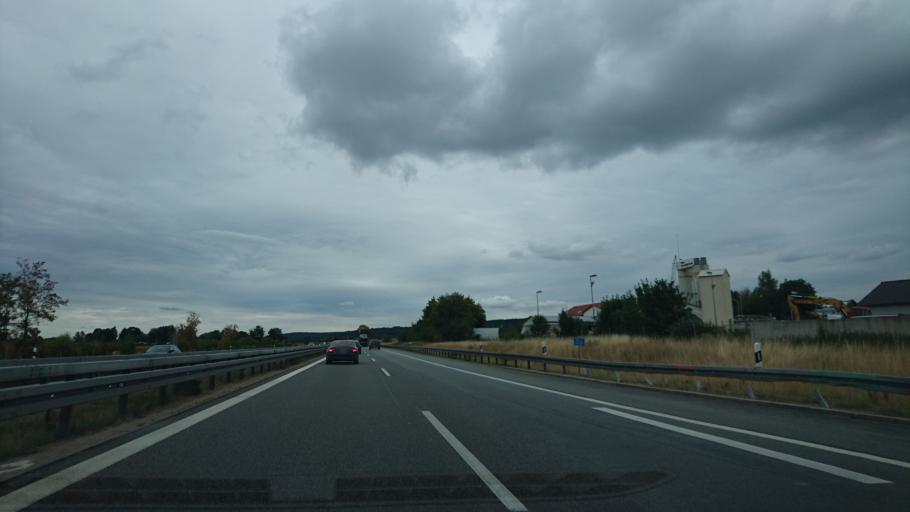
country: DE
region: Bavaria
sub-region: Upper Palatinate
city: Nabburg
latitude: 49.4569
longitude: 12.1944
